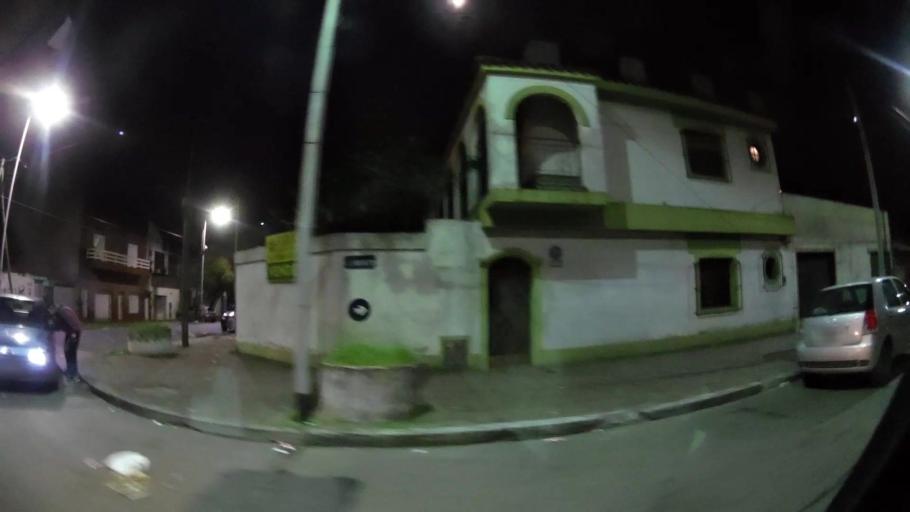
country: AR
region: Buenos Aires
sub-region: Partido de Avellaneda
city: Avellaneda
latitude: -34.7130
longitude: -58.3263
